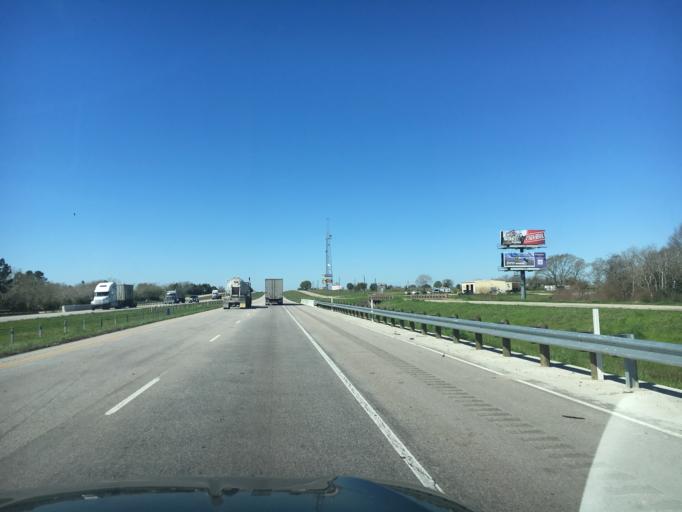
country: US
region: Texas
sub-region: Colorado County
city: Eagle Lake
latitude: 29.7353
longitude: -96.3620
